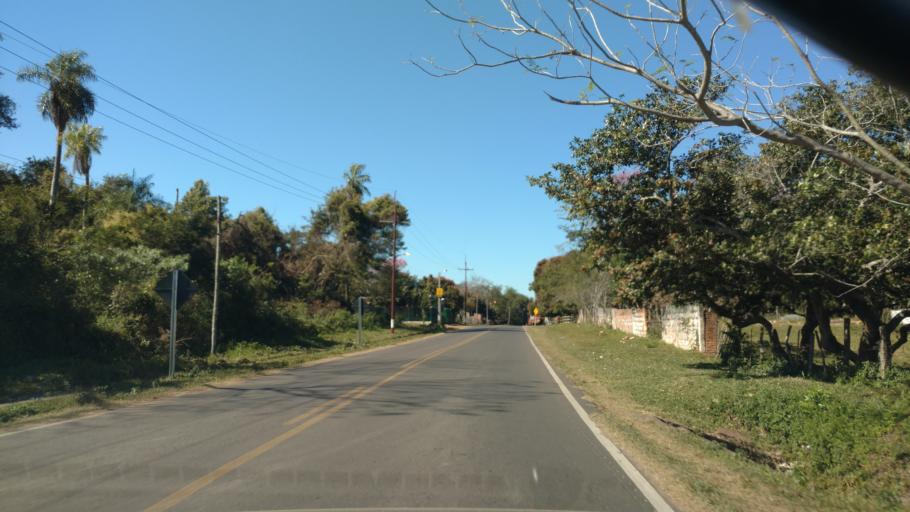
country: PY
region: Central
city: Ypacarai
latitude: -25.4294
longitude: -57.2863
